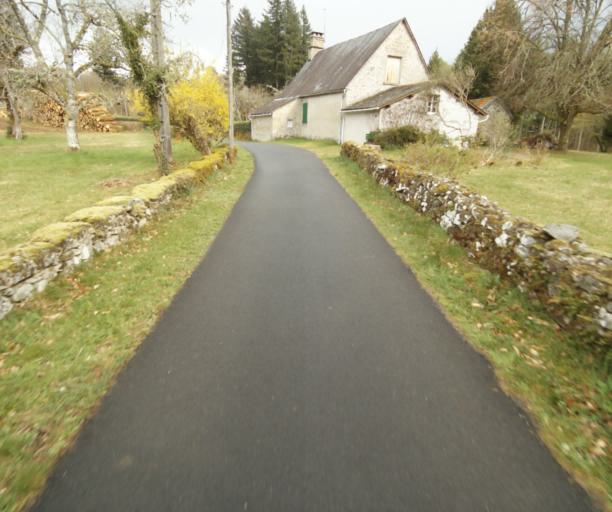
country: FR
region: Limousin
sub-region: Departement de la Correze
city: Saint-Privat
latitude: 45.2187
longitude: 1.9953
